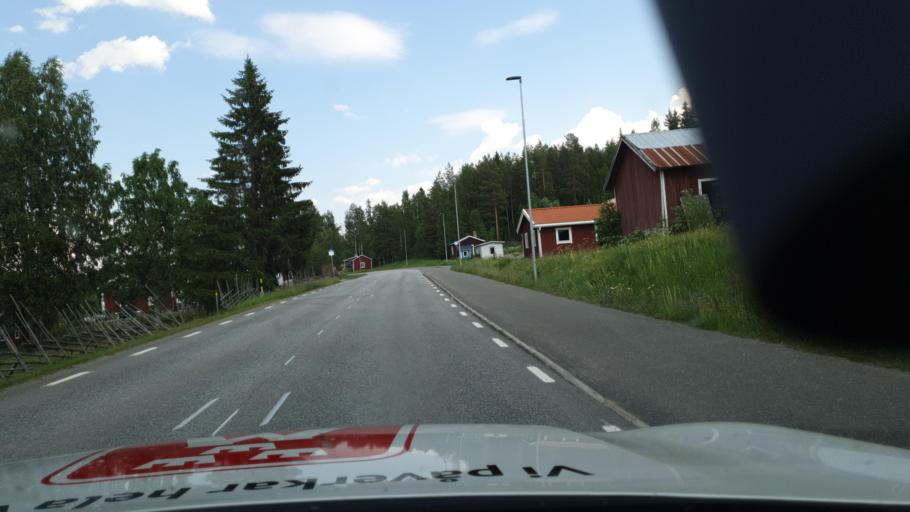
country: SE
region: Vaesterbotten
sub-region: Skelleftea Kommun
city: Viken
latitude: 64.7302
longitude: 20.7234
